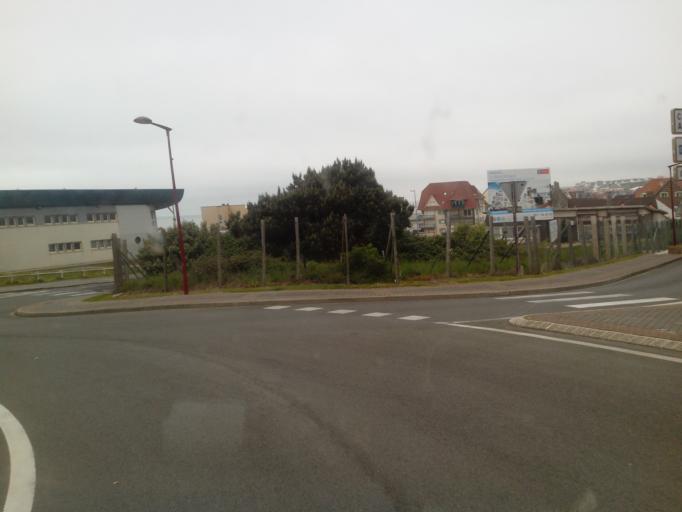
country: FR
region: Nord-Pas-de-Calais
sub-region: Departement du Pas-de-Calais
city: Wimereux
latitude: 50.7616
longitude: 1.6065
